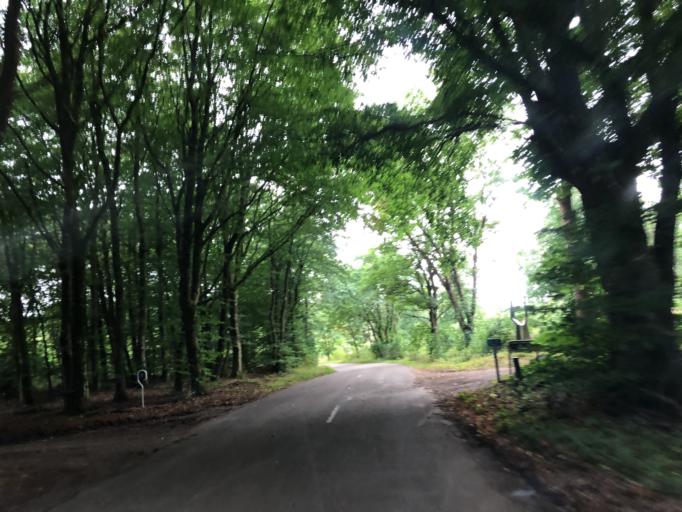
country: DK
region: Central Jutland
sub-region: Herning Kommune
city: Lind
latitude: 56.0764
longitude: 8.9742
